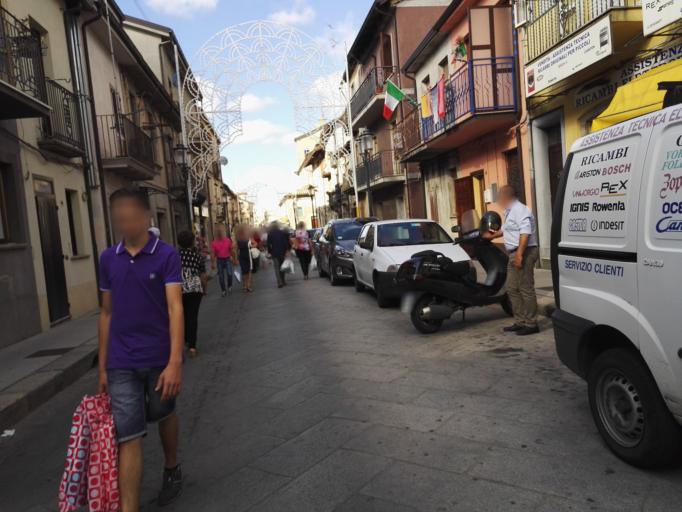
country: IT
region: Calabria
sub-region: Provincia di Vibo-Valentia
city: Serra San Bruno
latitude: 38.5750
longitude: 16.3286
